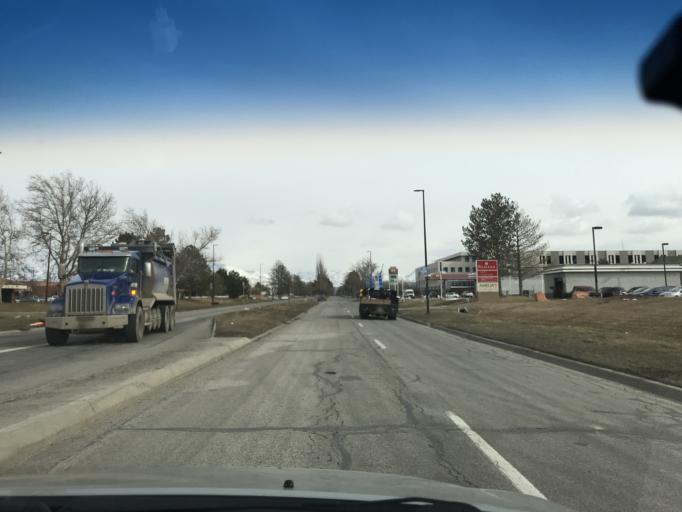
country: US
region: Utah
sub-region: Salt Lake County
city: West Valley City
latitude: 40.7763
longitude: -112.0244
